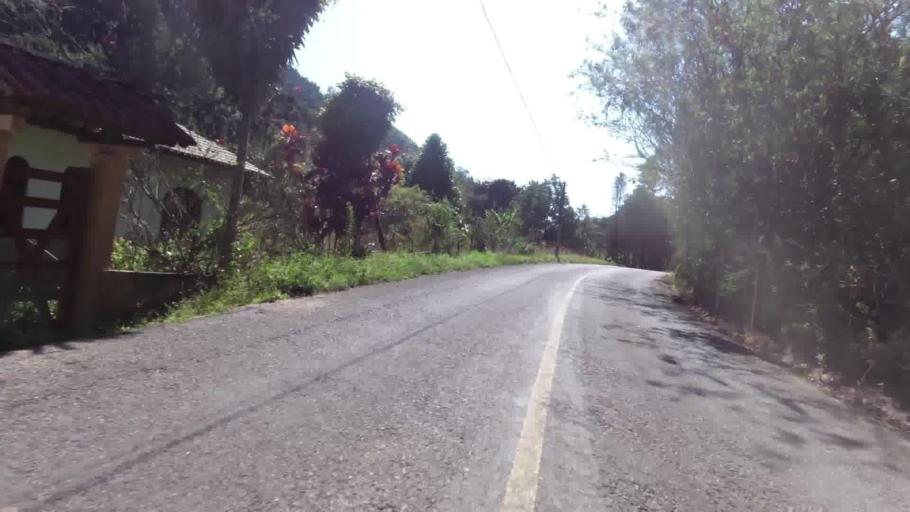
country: BR
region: Espirito Santo
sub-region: Marechal Floriano
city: Marechal Floriano
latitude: -20.4456
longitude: -40.8861
